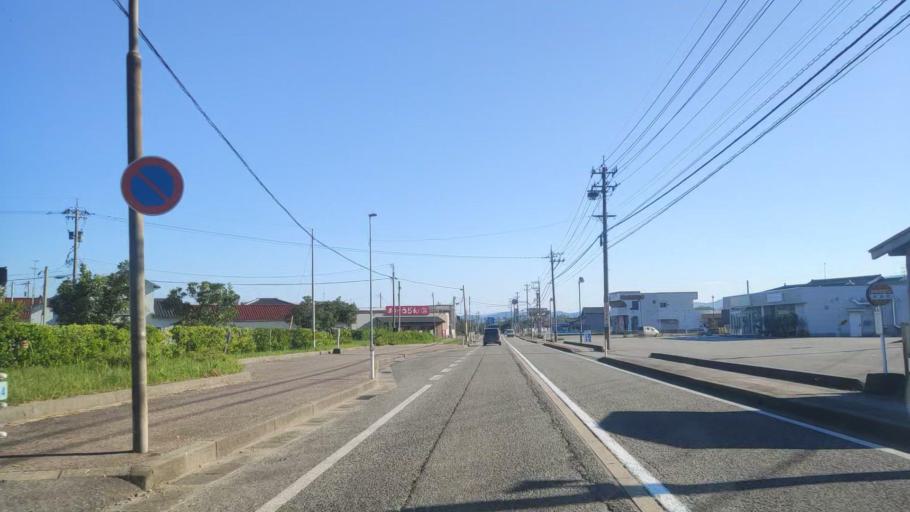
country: JP
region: Ishikawa
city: Tsubata
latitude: 36.7758
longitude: 136.7316
